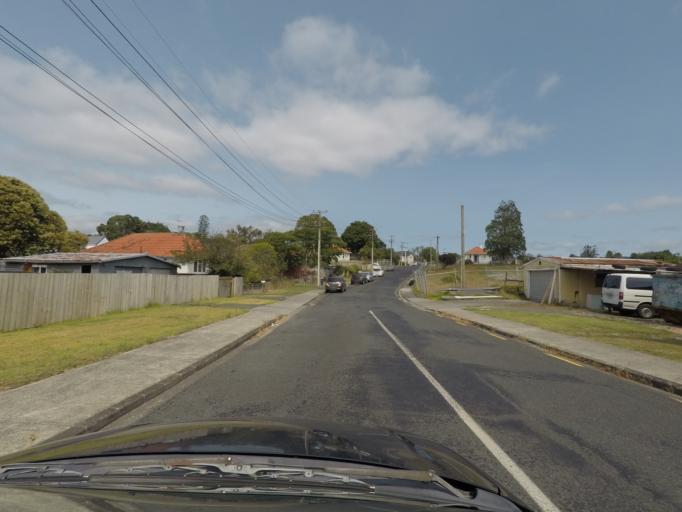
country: NZ
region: Auckland
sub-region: Auckland
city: Waitakere
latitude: -36.9154
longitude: 174.6907
